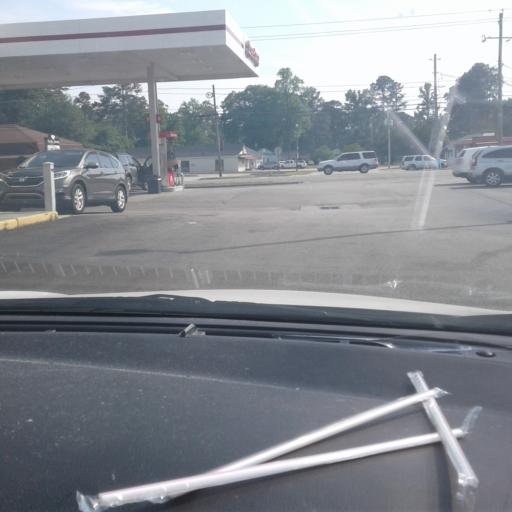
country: US
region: North Carolina
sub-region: Harnett County
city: Dunn
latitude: 35.3149
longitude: -78.6232
